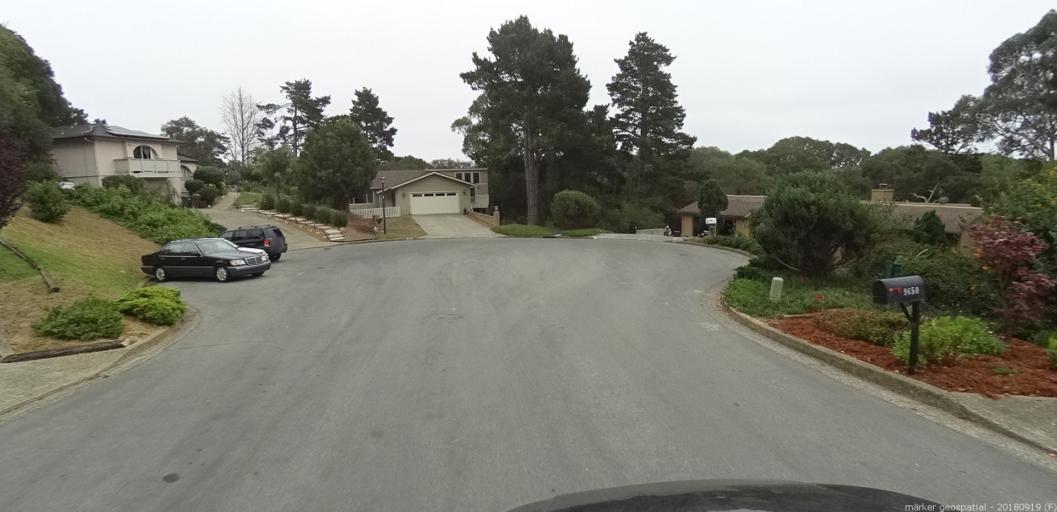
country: US
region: California
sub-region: Monterey County
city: Castroville
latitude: 36.7767
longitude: -121.7185
